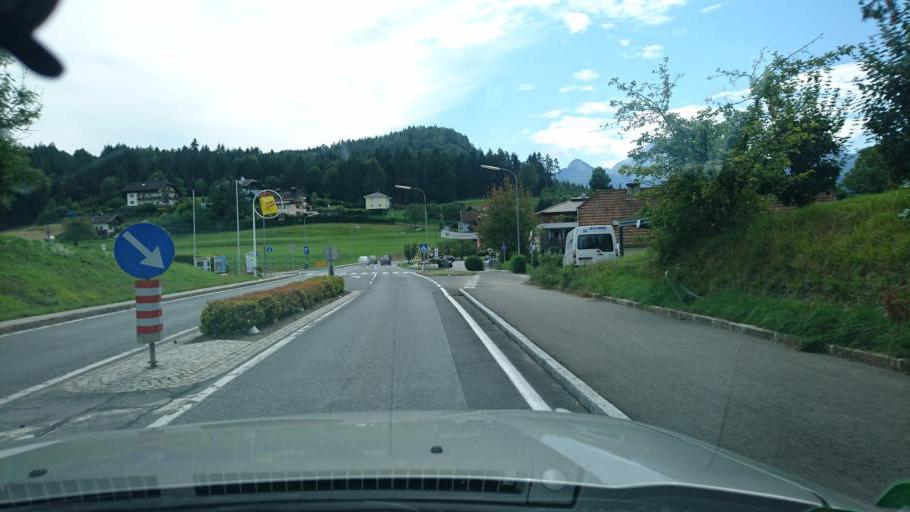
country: AT
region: Carinthia
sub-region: Politischer Bezirk Villach Land
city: Wernberg
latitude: 46.5881
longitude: 13.9342
